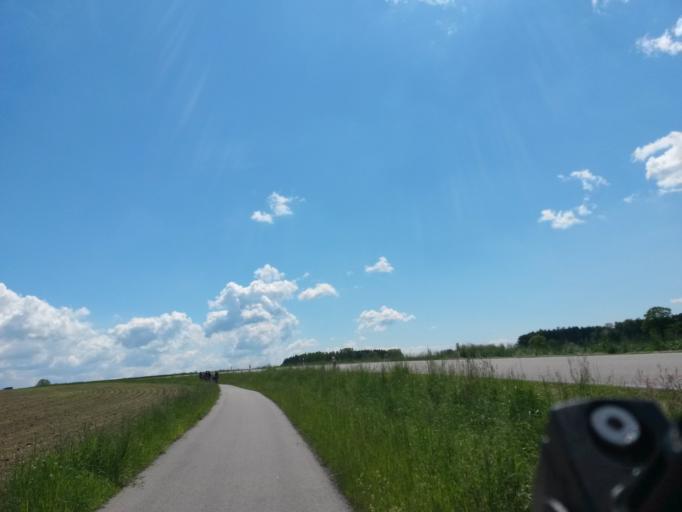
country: DE
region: Baden-Wuerttemberg
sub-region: Tuebingen Region
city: Bad Waldsee
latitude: 47.9483
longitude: 9.7437
